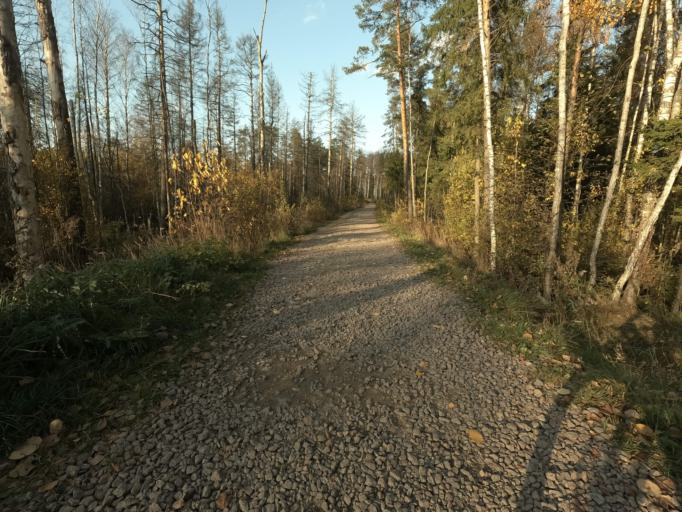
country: RU
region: Leningrad
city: Sertolovo
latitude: 60.1487
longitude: 30.2223
